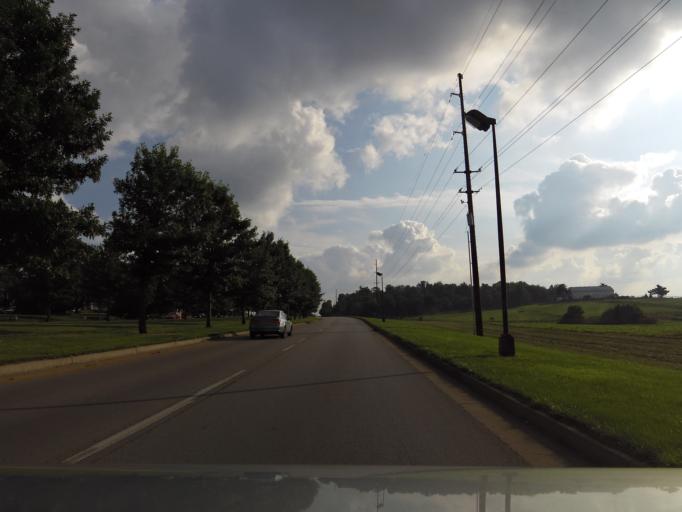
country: US
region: Kentucky
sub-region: Bourbon County
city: Paris
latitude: 38.1887
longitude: -84.2851
